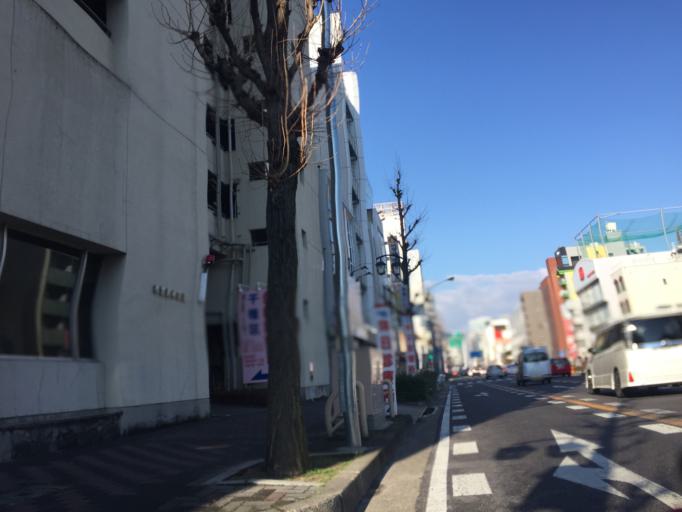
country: JP
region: Aichi
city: Nagoya-shi
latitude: 35.1683
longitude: 136.9403
